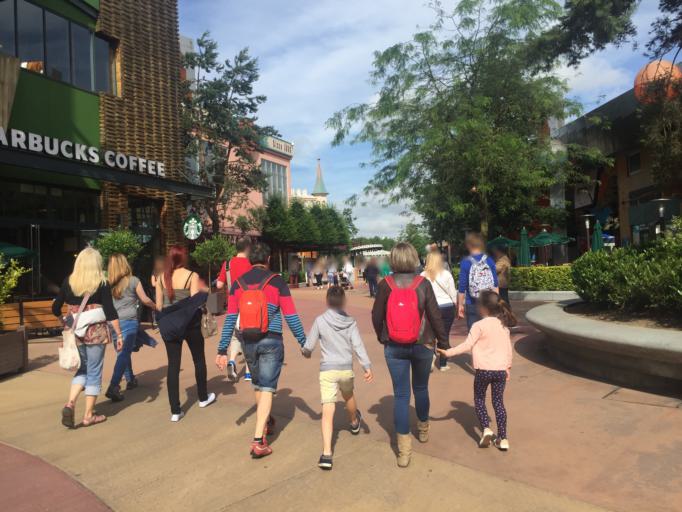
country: FR
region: Ile-de-France
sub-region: Departement de Seine-et-Marne
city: Chessy
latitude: 48.8692
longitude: 2.7852
